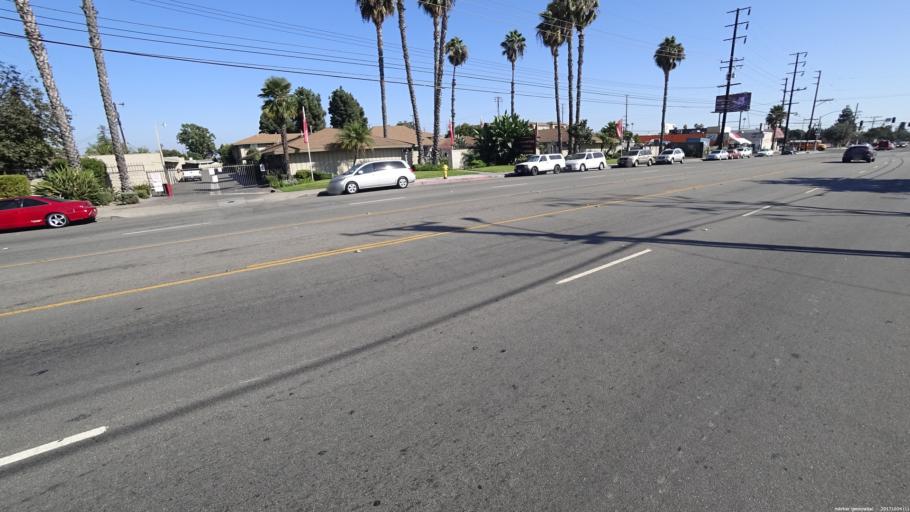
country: US
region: California
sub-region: Orange County
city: Stanton
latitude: 33.8045
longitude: -117.9758
